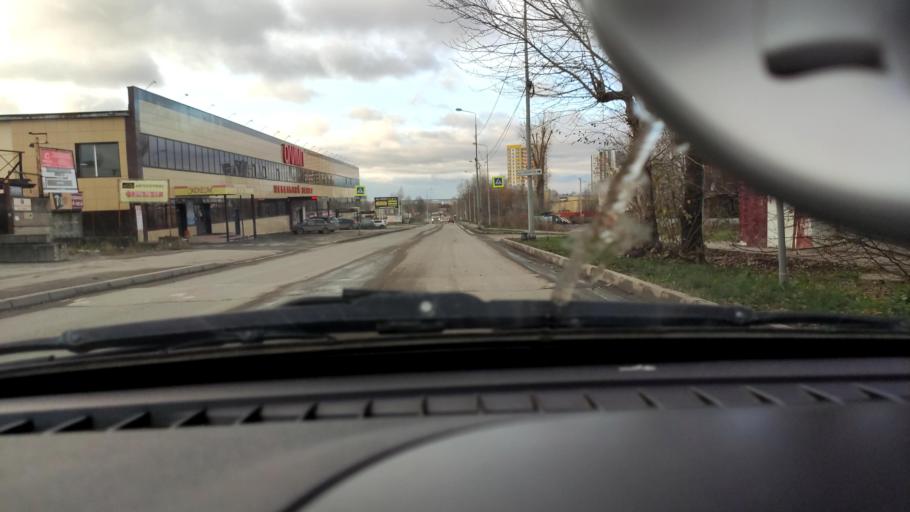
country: RU
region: Perm
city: Kondratovo
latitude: 57.9613
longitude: 56.1635
